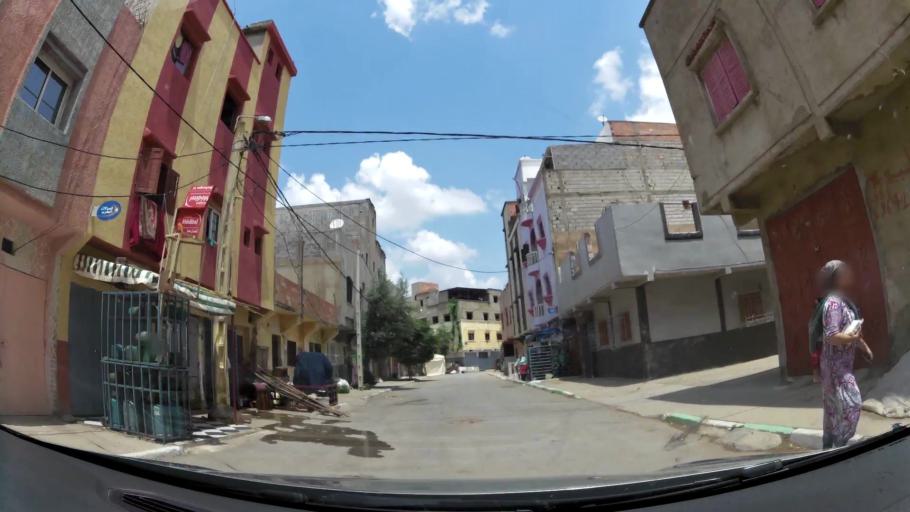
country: MA
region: Rabat-Sale-Zemmour-Zaer
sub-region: Khemisset
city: Tiflet
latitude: 34.0003
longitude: -6.5296
